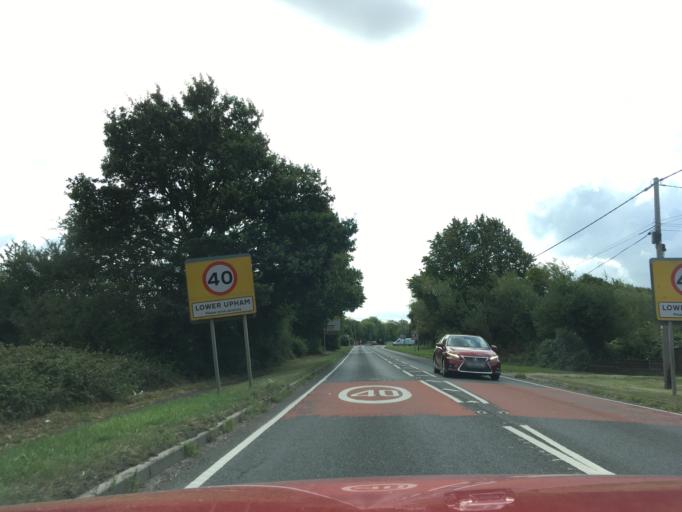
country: GB
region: England
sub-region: Hampshire
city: Bishops Waltham
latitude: 50.9744
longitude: -1.2593
